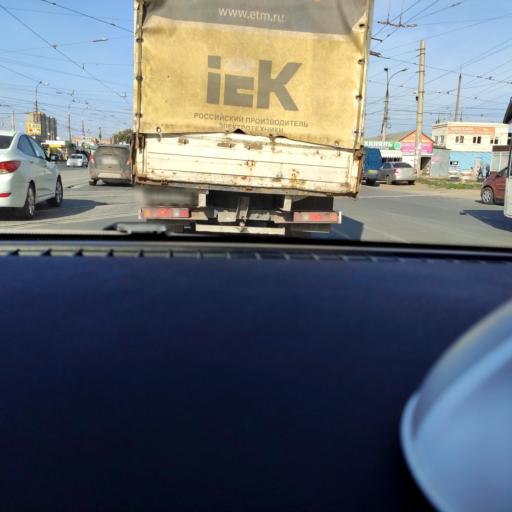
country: RU
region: Samara
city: Smyshlyayevka
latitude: 53.2089
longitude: 50.2753
